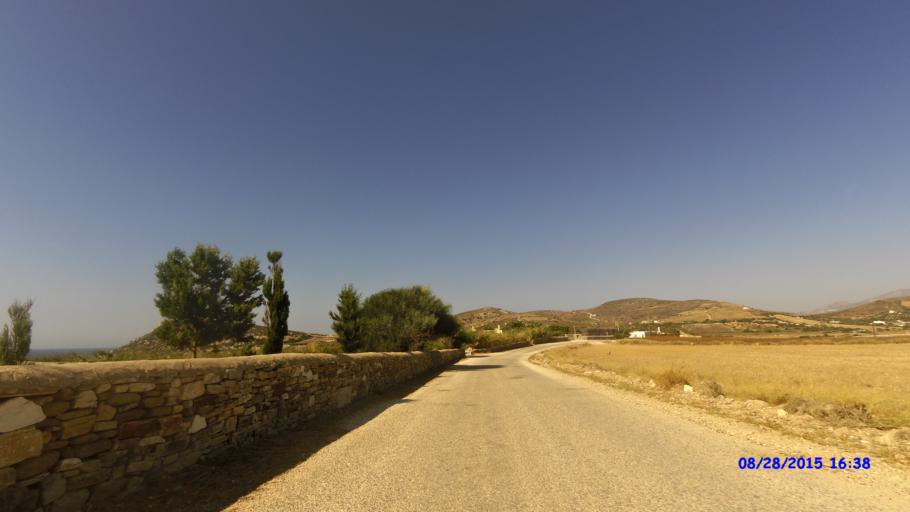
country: GR
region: South Aegean
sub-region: Nomos Kykladon
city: Antiparos
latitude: 37.0147
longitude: 25.0490
